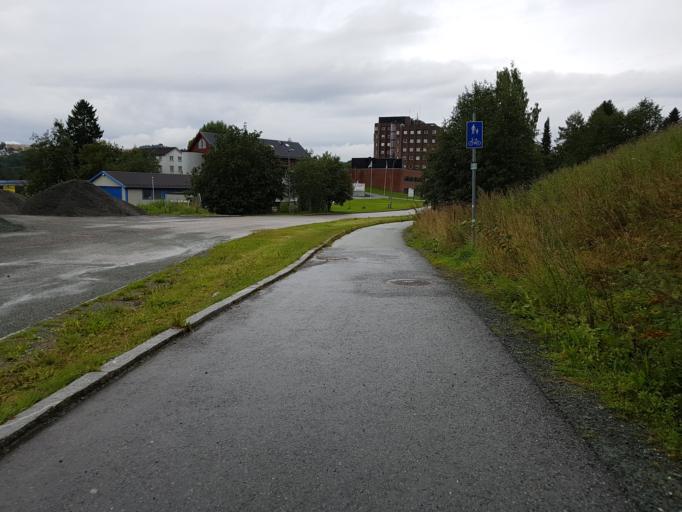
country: NO
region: Sor-Trondelag
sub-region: Trondheim
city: Trondheim
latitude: 63.3899
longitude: 10.4050
